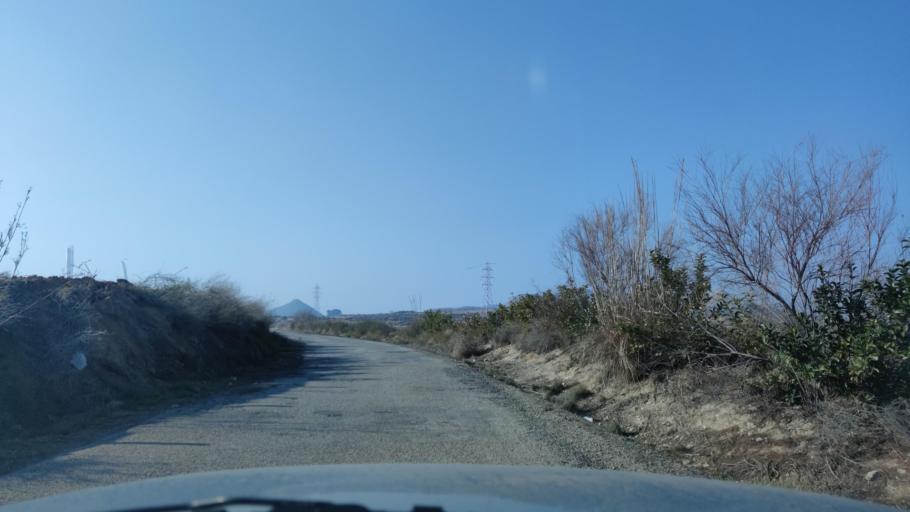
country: ES
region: Catalonia
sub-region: Provincia de Lleida
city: Seros
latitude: 41.4666
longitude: 0.3864
